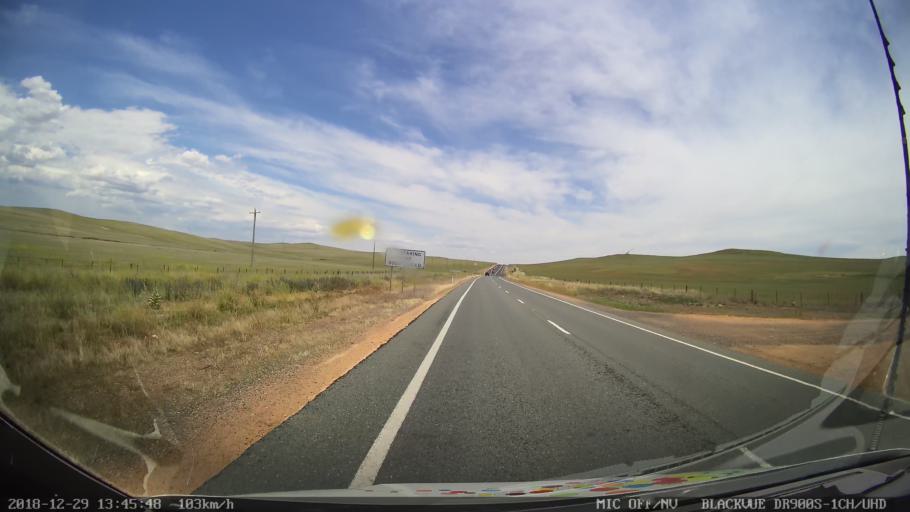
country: AU
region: New South Wales
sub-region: Cooma-Monaro
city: Cooma
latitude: -36.1021
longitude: 149.1449
